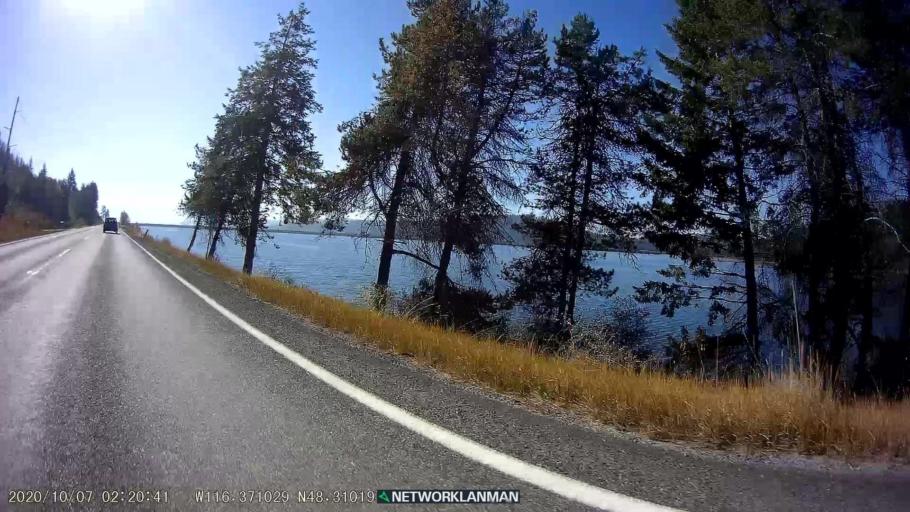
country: US
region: Idaho
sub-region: Bonner County
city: Ponderay
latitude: 48.3100
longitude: -116.3711
